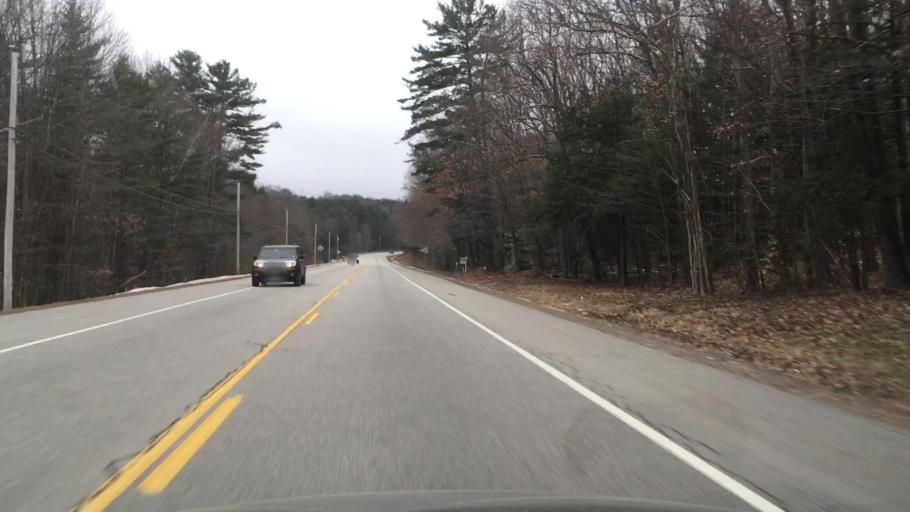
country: US
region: New Hampshire
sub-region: Hillsborough County
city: Weare
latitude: 43.0631
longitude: -71.7168
